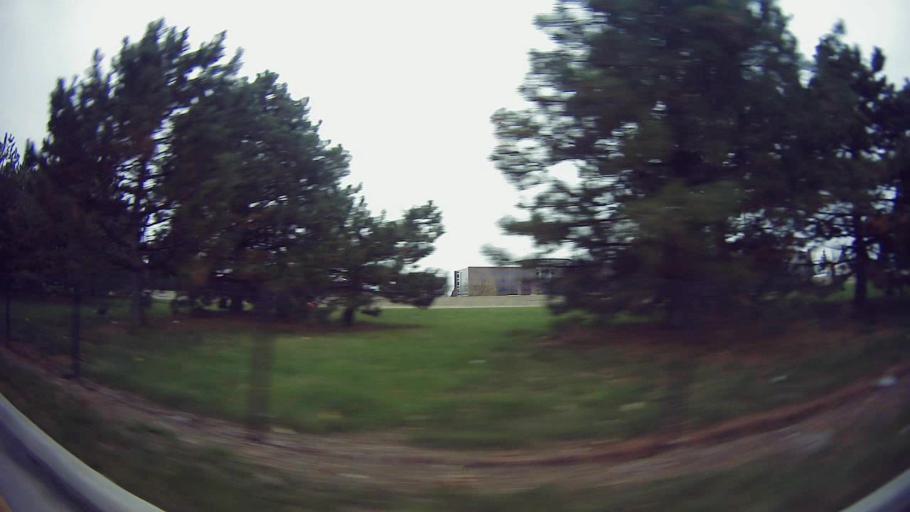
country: US
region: Michigan
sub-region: Wayne County
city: Dearborn
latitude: 42.3153
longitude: -83.2146
